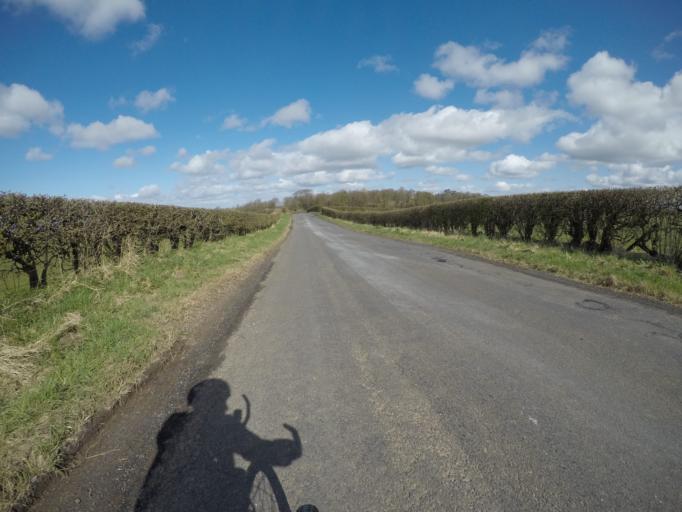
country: GB
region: Scotland
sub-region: East Ayrshire
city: Crosshouse
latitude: 55.6085
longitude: -4.5759
